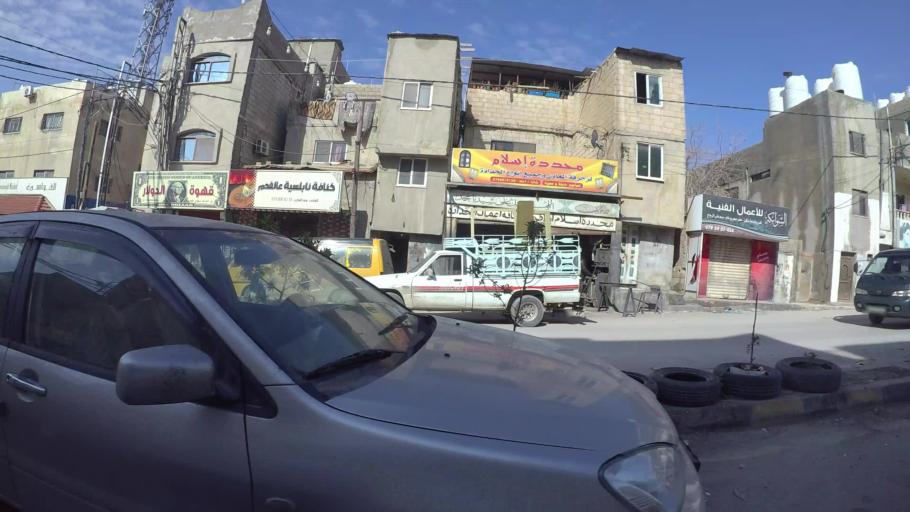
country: JO
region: Amman
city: Al Jubayhah
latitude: 32.0678
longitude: 35.8427
